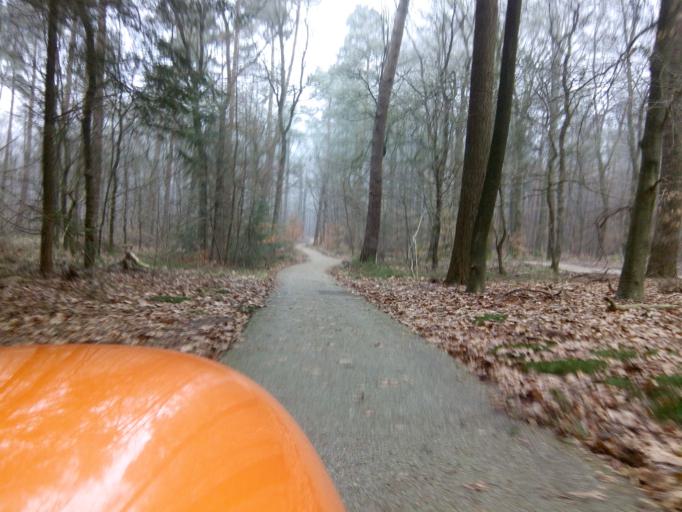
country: NL
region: Gelderland
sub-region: Gemeente Putten
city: Putten
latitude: 52.2603
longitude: 5.6375
